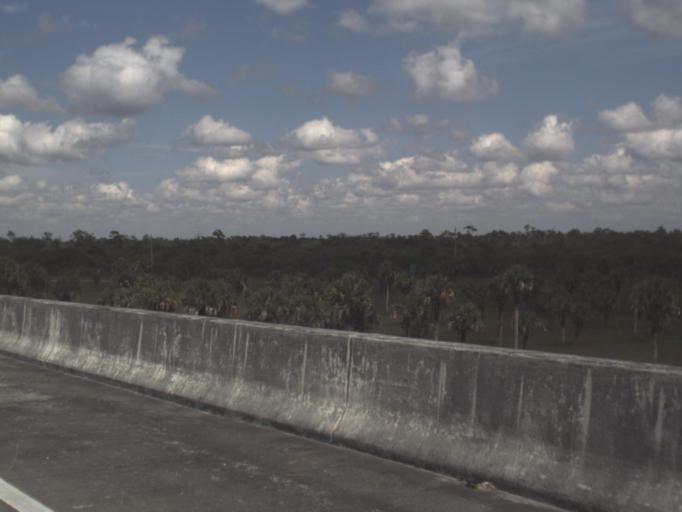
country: US
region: Florida
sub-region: Collier County
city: Immokalee
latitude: 26.1549
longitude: -81.3450
